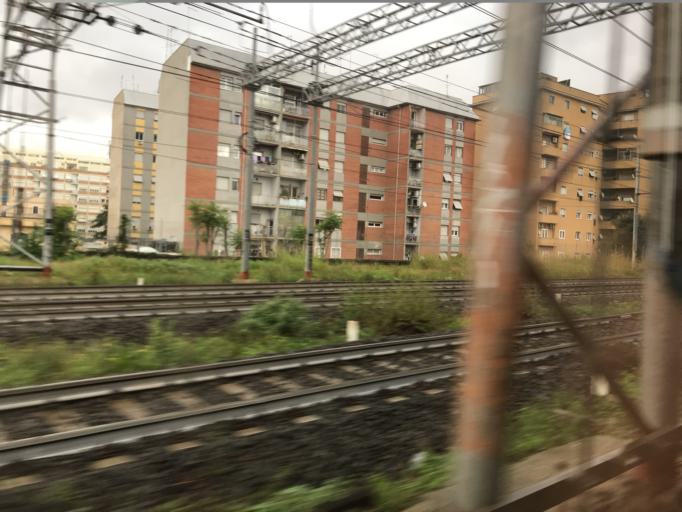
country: VA
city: Vatican City
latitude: 41.8723
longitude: 12.4689
